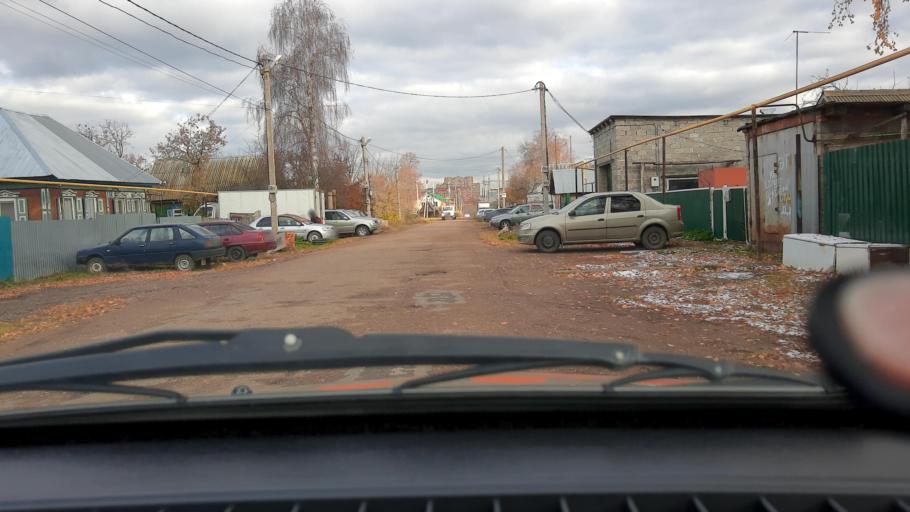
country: RU
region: Bashkortostan
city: Ufa
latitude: 54.7800
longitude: 56.0621
